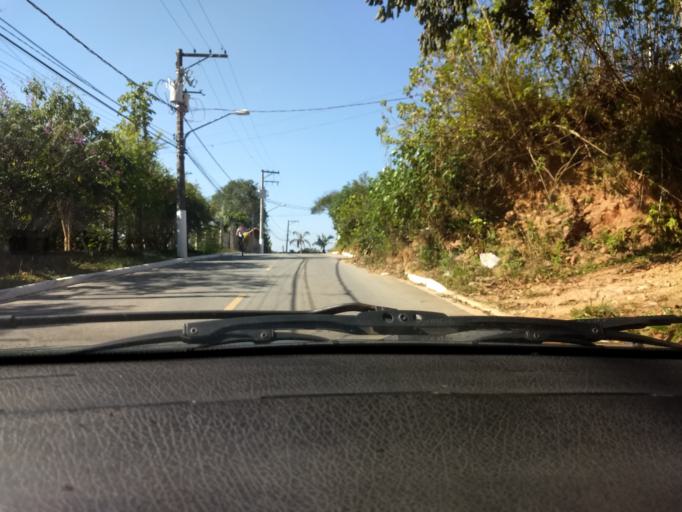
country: BR
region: Sao Paulo
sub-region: Embu-Guacu
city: Embu Guacu
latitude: -23.8033
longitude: -46.7401
